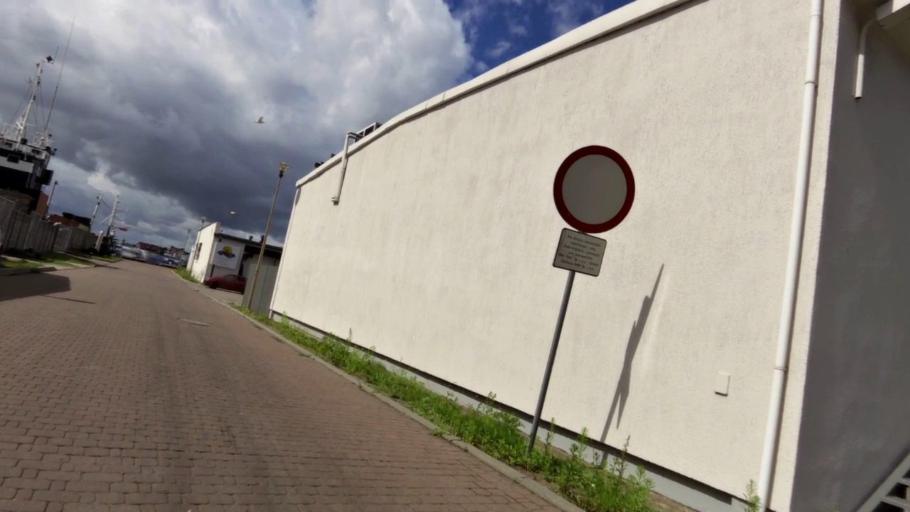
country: PL
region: West Pomeranian Voivodeship
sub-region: Powiat slawienski
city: Darlowo
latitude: 54.4385
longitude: 16.3854
